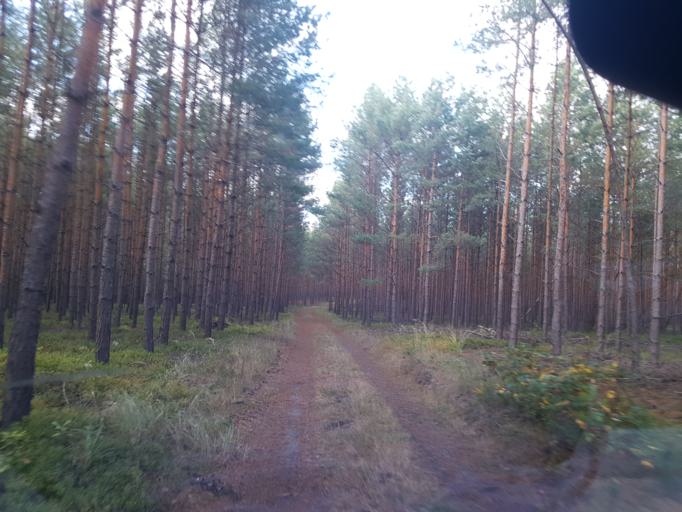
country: DE
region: Brandenburg
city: Finsterwalde
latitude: 51.5578
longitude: 13.6982
